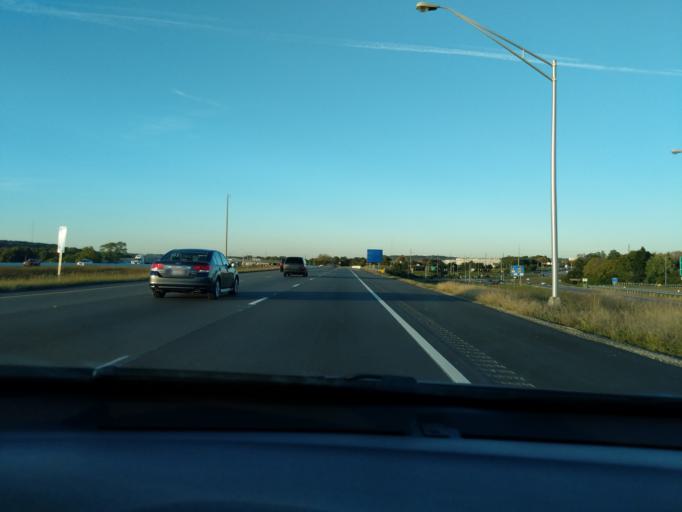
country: US
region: Ohio
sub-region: Montgomery County
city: West Carrollton City
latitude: 39.6791
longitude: -84.2306
